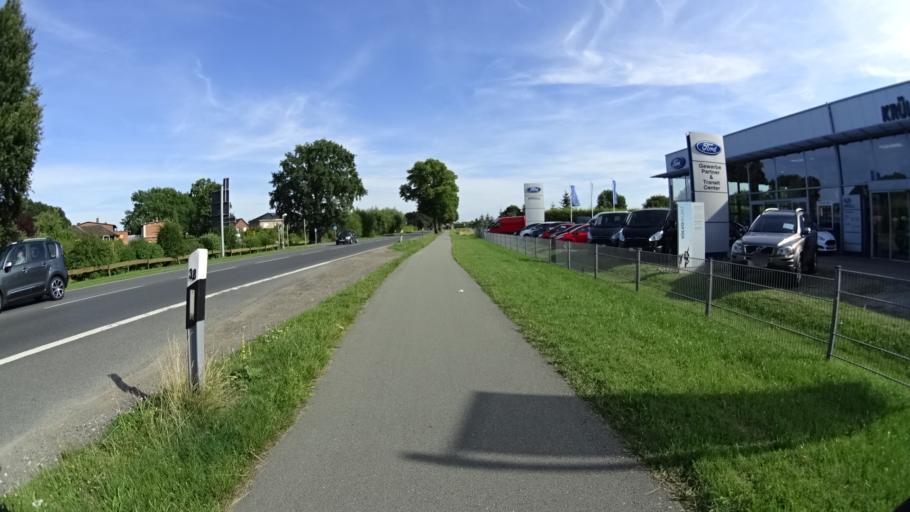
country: DE
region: Lower Saxony
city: Bardowick
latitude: 53.2836
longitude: 10.3958
